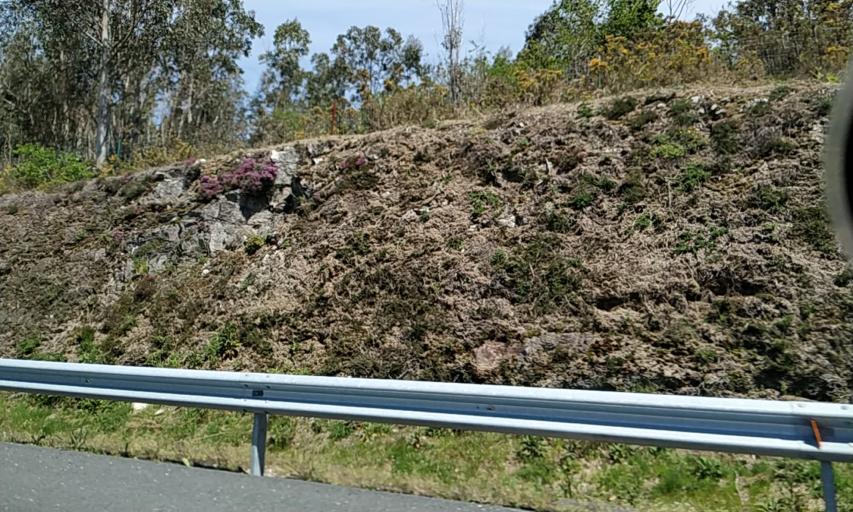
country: ES
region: Galicia
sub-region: Provincia da Coruna
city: Santiago de Compostela
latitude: 42.8427
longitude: -8.5713
